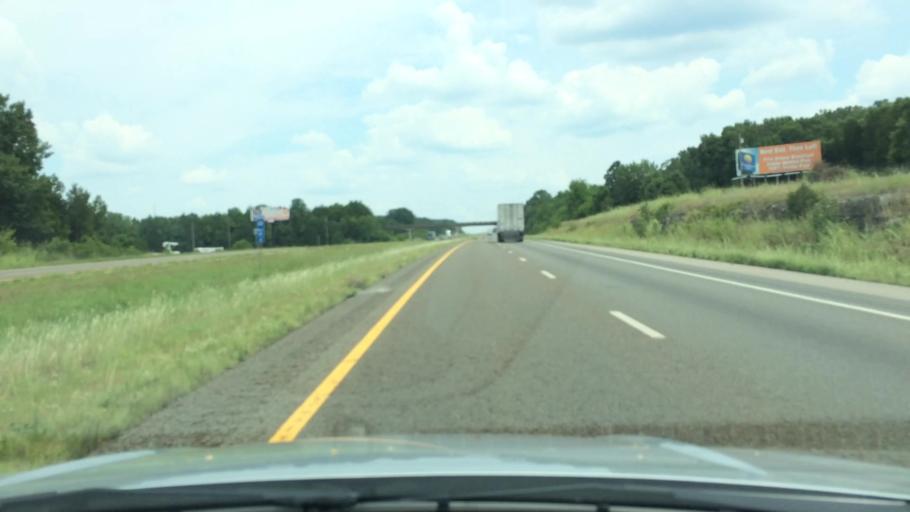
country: US
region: Tennessee
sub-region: Maury County
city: Spring Hill
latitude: 35.6209
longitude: -86.8992
